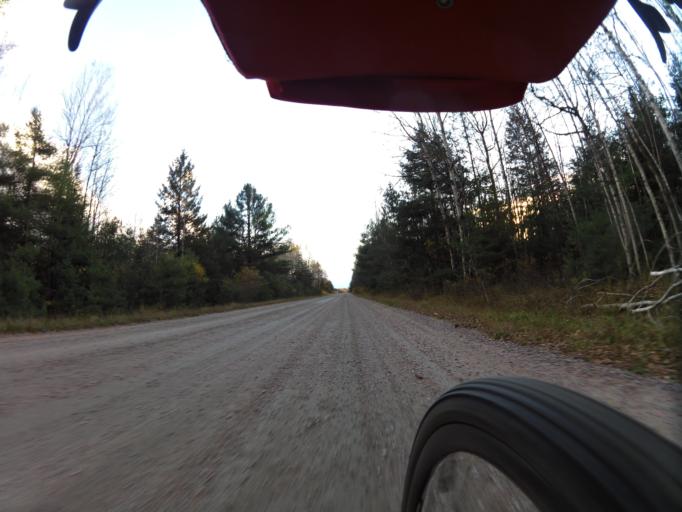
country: CA
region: Quebec
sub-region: Outaouais
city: Shawville
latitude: 45.6551
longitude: -76.3153
